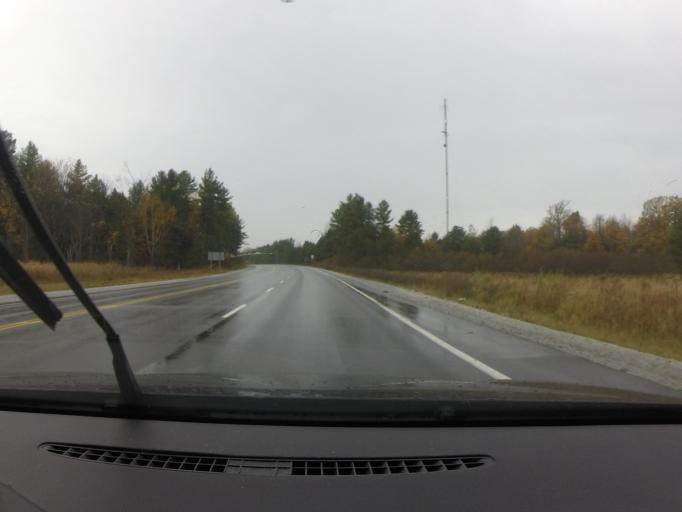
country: CA
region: Ontario
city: Perth
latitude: 44.8507
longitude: -76.4675
